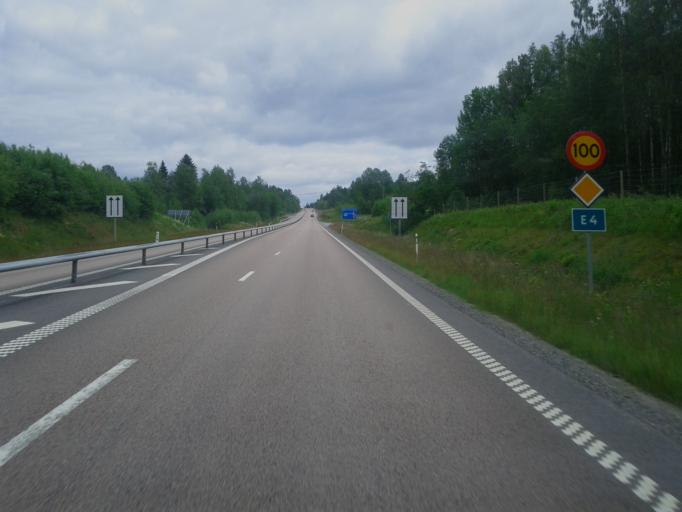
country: SE
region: Vaesternorrland
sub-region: OErnskoeldsviks Kommun
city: Bjasta
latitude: 63.1773
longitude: 18.4416
